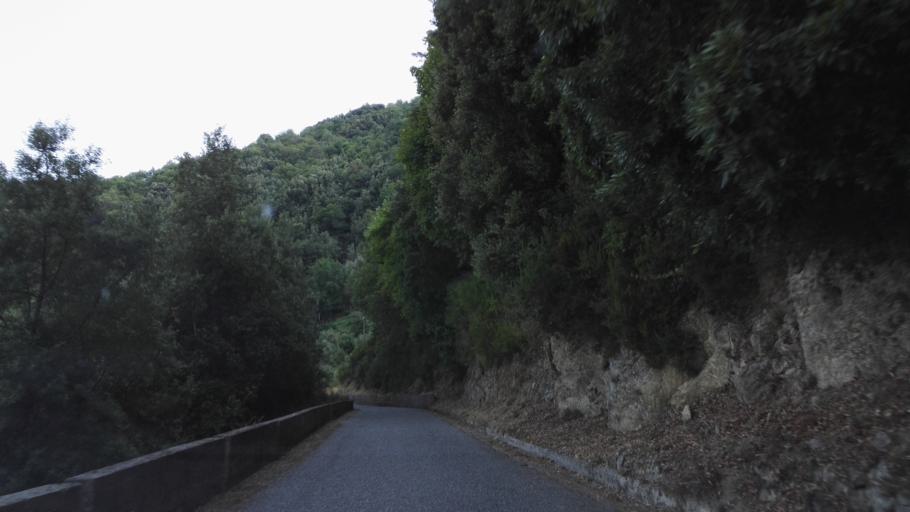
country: IT
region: Calabria
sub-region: Provincia di Vibo-Valentia
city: Nardodipace
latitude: 38.4449
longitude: 16.3408
